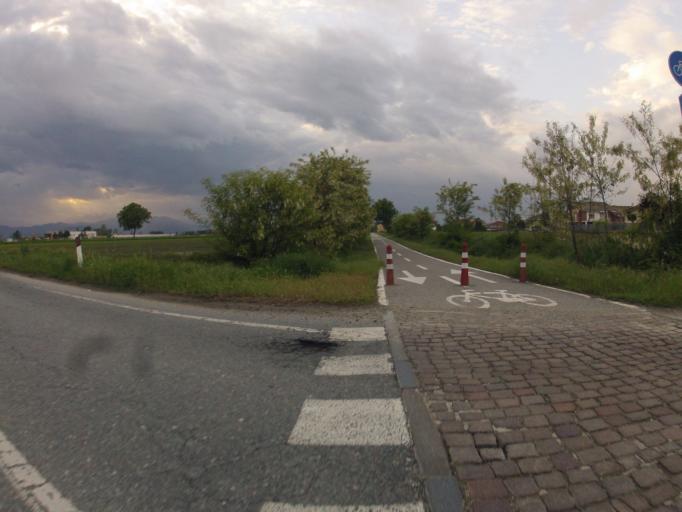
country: IT
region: Piedmont
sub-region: Provincia di Torino
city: Vigone
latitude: 44.8344
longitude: 7.4922
